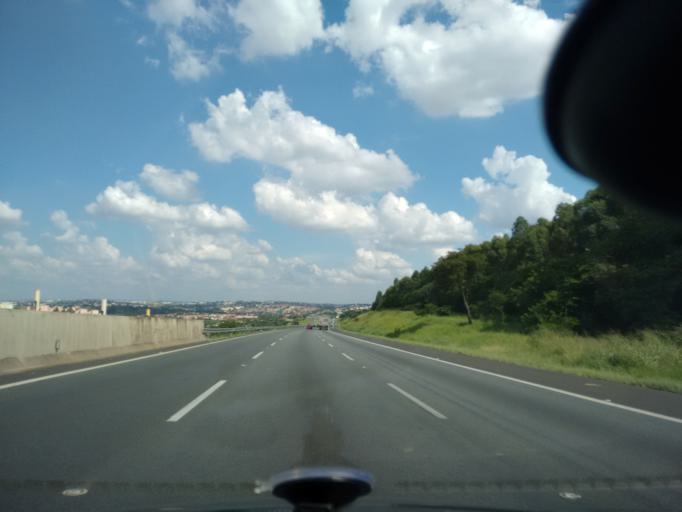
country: BR
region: Sao Paulo
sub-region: Campinas
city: Campinas
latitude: -22.9417
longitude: -47.1262
